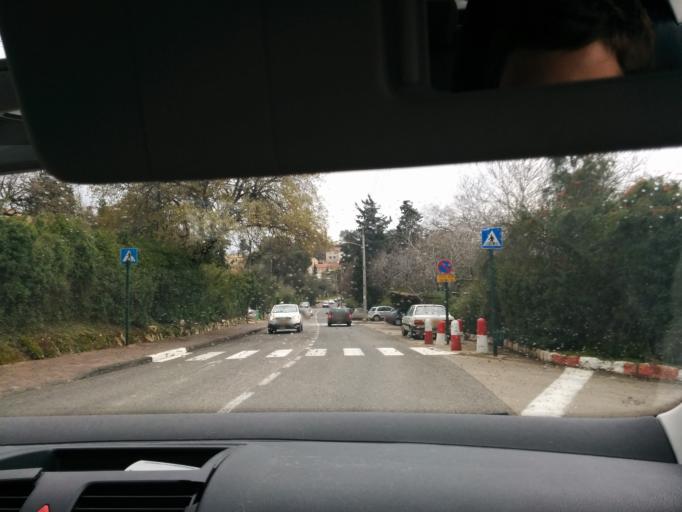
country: IL
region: Northern District
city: Basmat Tab`un
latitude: 32.7248
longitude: 35.1343
